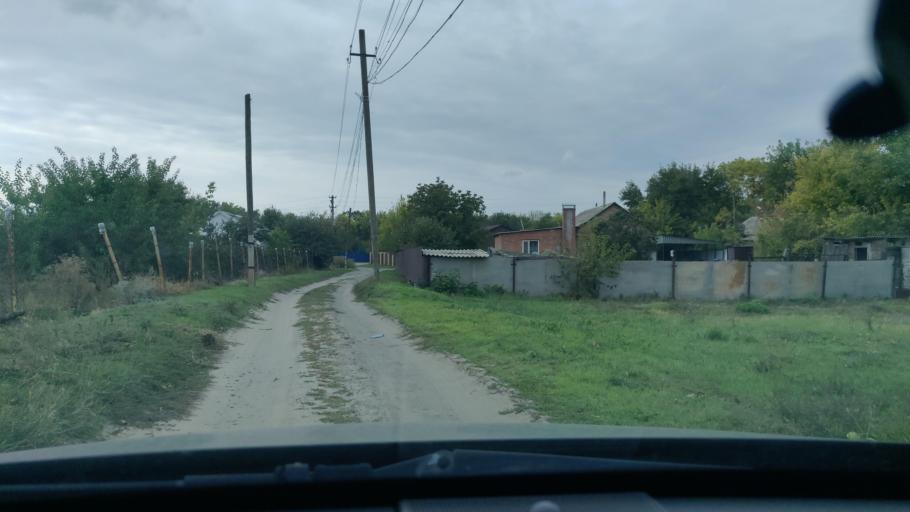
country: RU
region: Rostov
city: Ust'-Donetskiy
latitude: 47.6592
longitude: 40.9190
